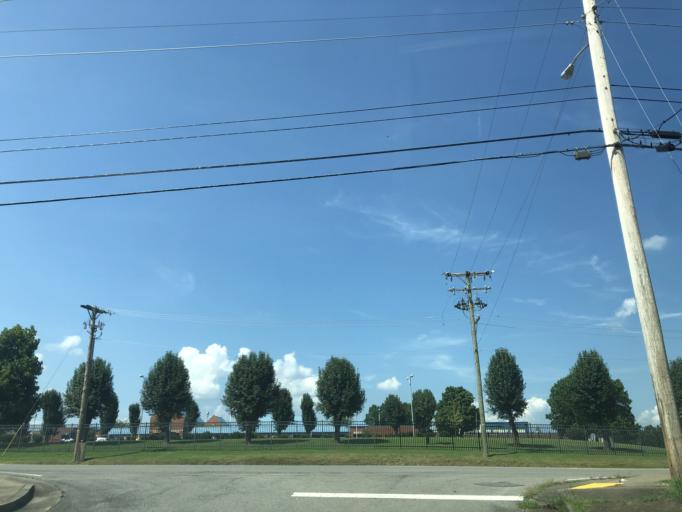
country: US
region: Tennessee
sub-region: Davidson County
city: Lakewood
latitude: 36.1660
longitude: -86.6542
